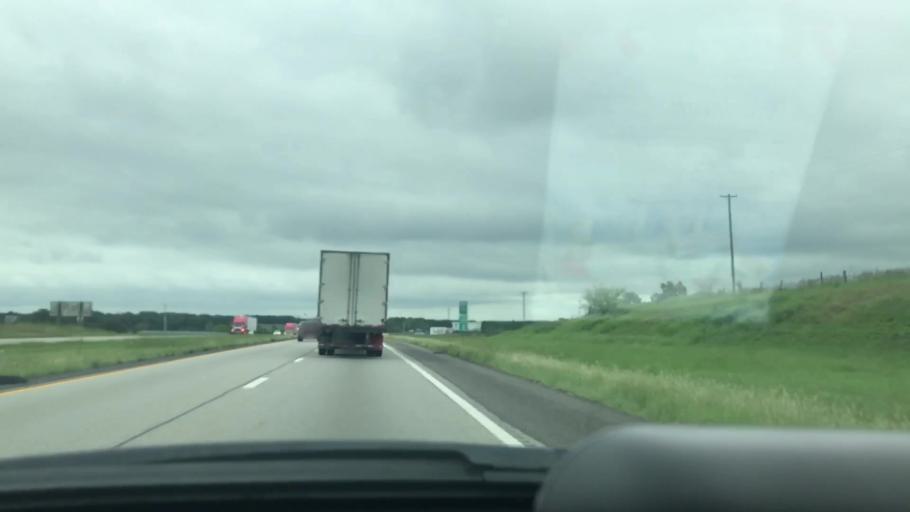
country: US
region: Missouri
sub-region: Christian County
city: Billings
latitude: 37.1850
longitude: -93.5903
